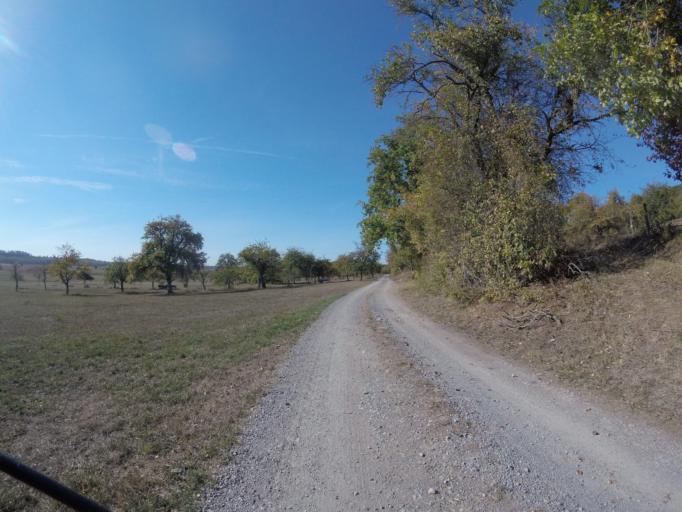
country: DE
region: Baden-Wuerttemberg
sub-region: Karlsruhe Region
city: Sternenfels
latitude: 49.0144
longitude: 8.8485
